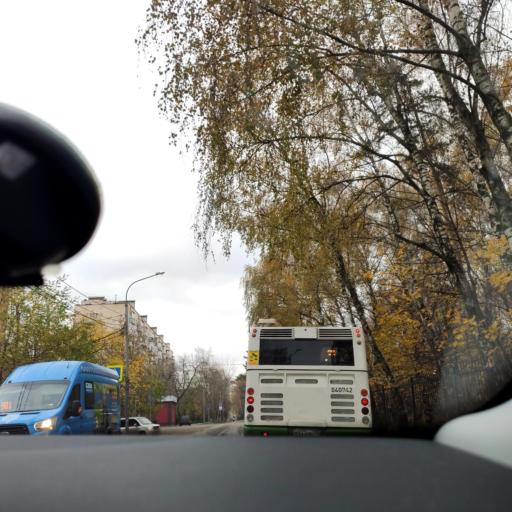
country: RU
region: Moscow
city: Kuz'minki
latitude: 55.6728
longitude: 37.8095
